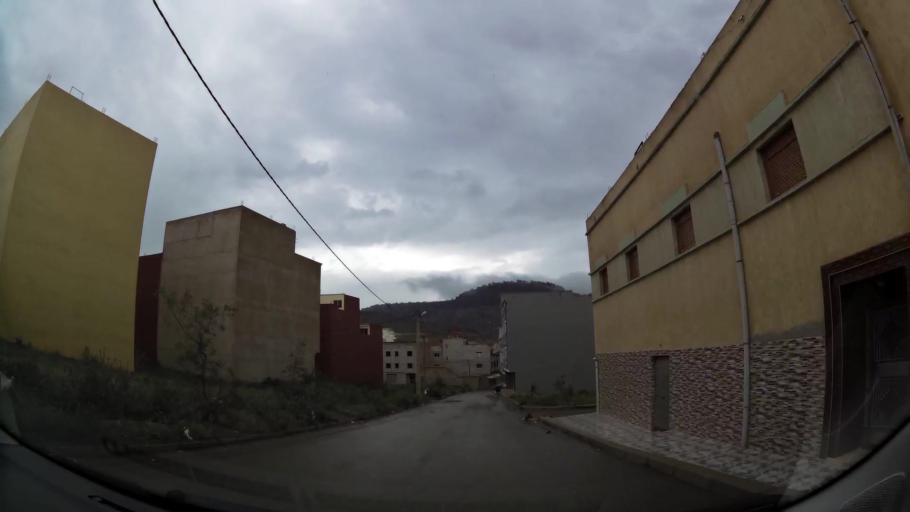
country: MA
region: Oriental
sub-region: Nador
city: Nador
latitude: 35.1470
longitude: -3.0035
